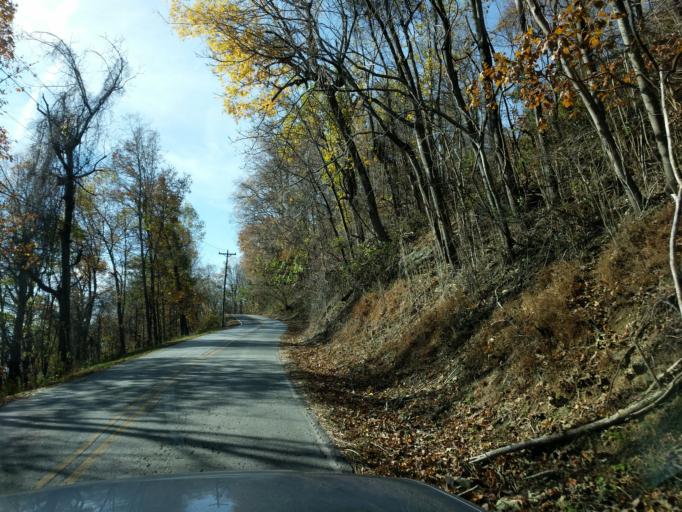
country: US
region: North Carolina
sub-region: Polk County
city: Columbus
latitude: 35.2714
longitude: -82.2186
